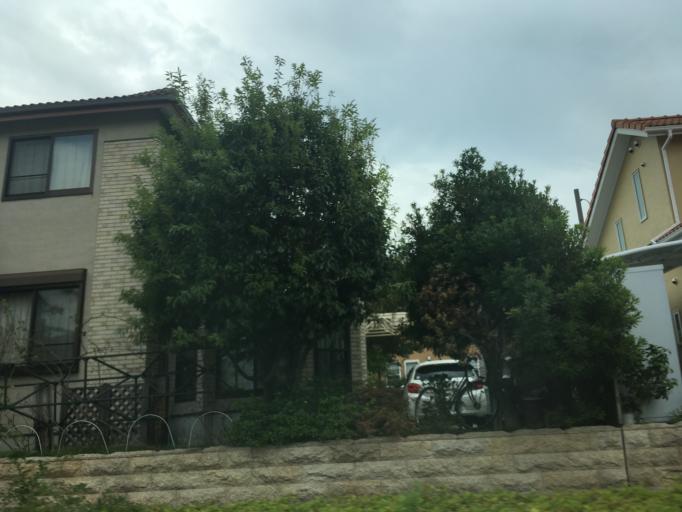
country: JP
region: Hyogo
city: Ashiya
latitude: 34.7113
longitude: 135.3103
